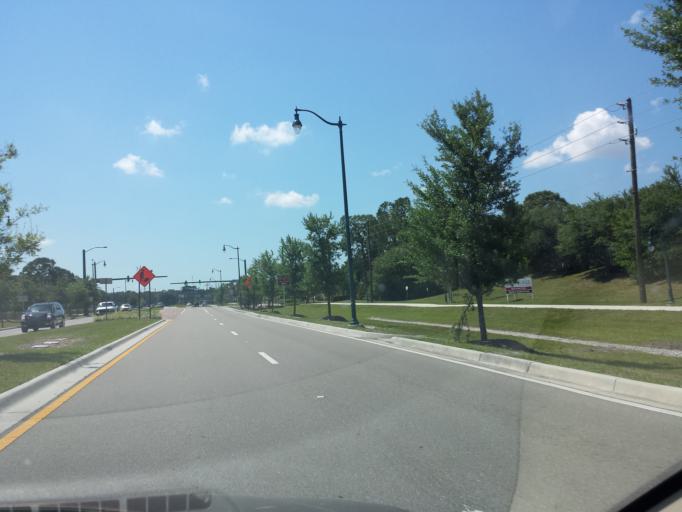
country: US
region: Florida
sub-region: Sarasota County
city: North Port
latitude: 27.0747
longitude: -82.2091
